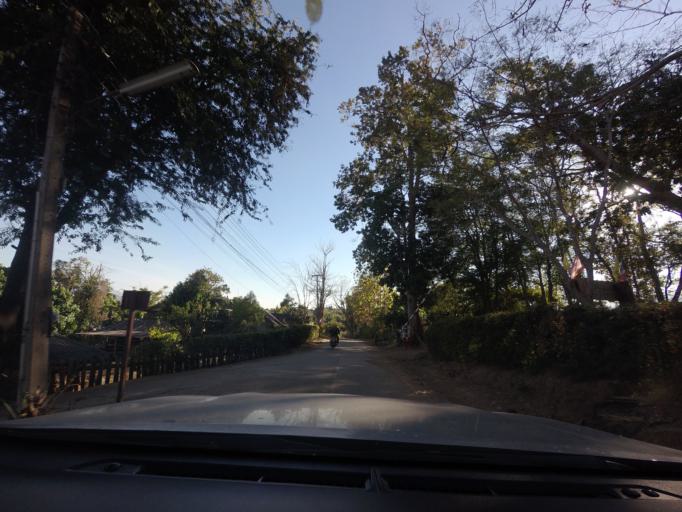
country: TH
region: Mae Hong Son
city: Wiang Nuea
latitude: 19.3980
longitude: 98.4217
